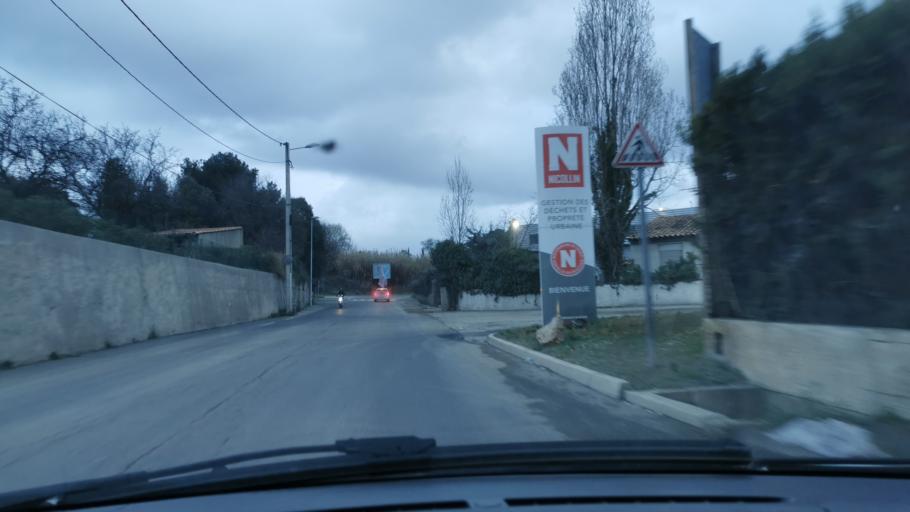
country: FR
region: Languedoc-Roussillon
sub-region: Departement de l'Herault
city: Montpellier
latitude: 43.5842
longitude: 3.8695
